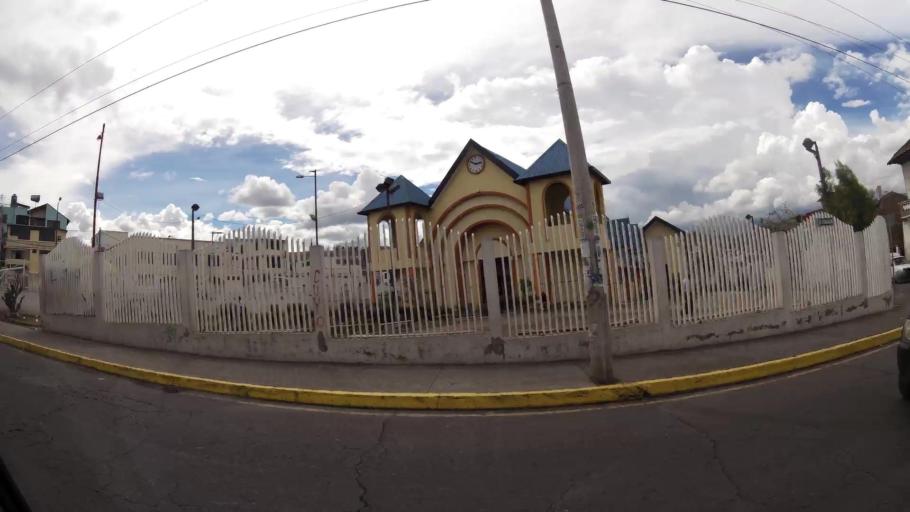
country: EC
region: Tungurahua
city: Ambato
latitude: -1.2737
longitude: -78.6298
